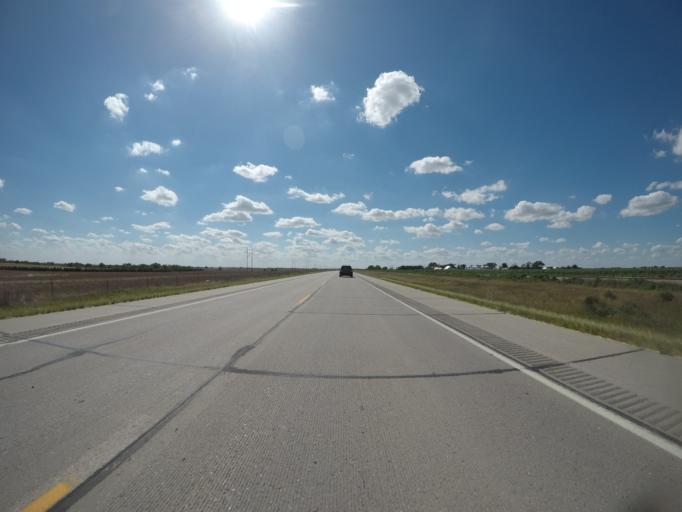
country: US
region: Colorado
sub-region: Phillips County
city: Holyoke
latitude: 40.5924
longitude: -102.3532
